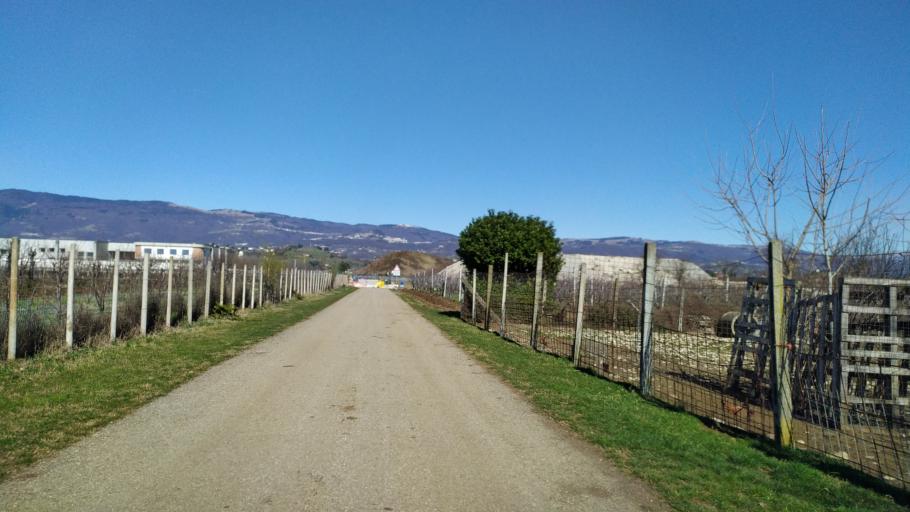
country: IT
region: Veneto
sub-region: Provincia di Vicenza
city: Breganze
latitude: 45.6928
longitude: 11.5687
